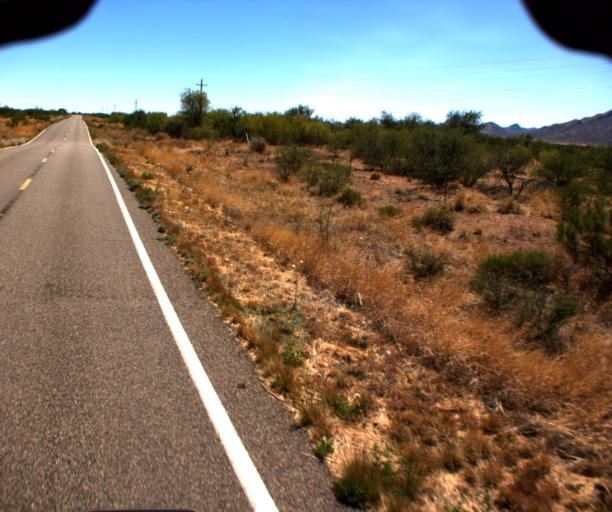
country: US
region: Arizona
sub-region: Pima County
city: Three Points
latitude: 31.7601
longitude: -111.4753
